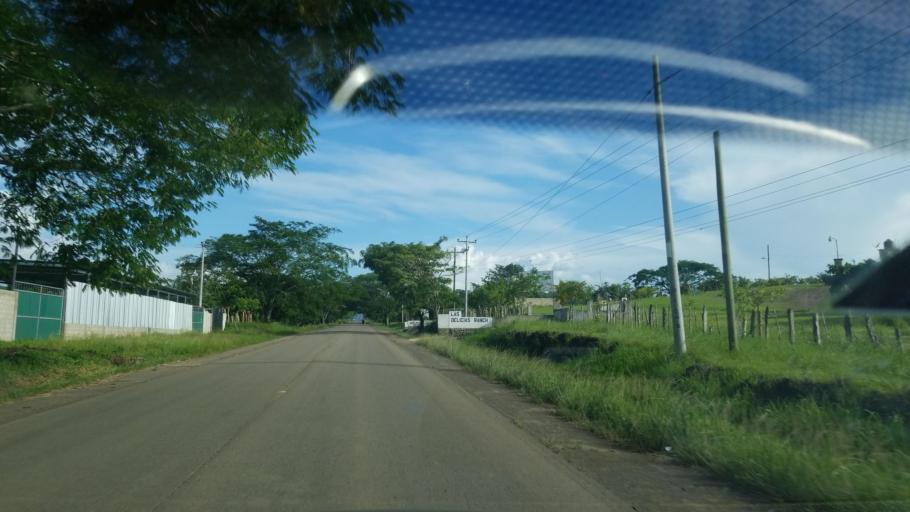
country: HN
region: El Paraiso
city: Arauli
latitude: 13.9224
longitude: -86.5578
